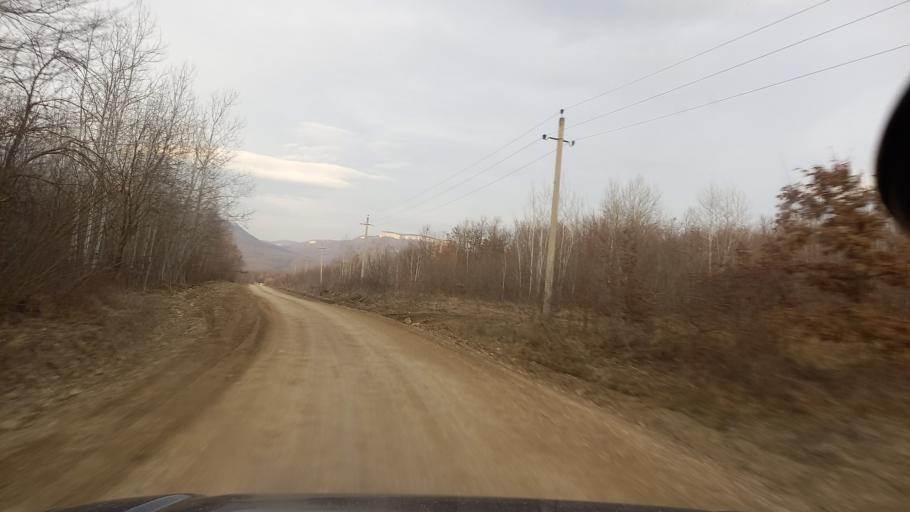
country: RU
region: Adygeya
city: Kamennomostskiy
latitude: 44.1791
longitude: 40.2580
